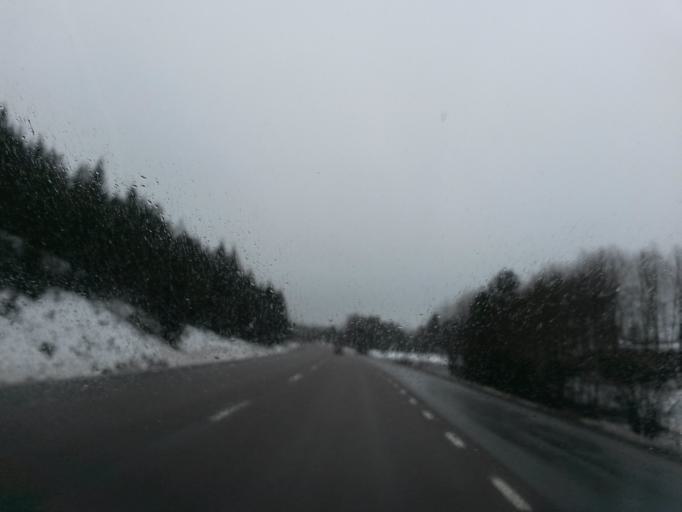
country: SE
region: Vaestra Goetaland
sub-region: Boras Kommun
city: Viskafors
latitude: 57.6433
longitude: 12.9090
